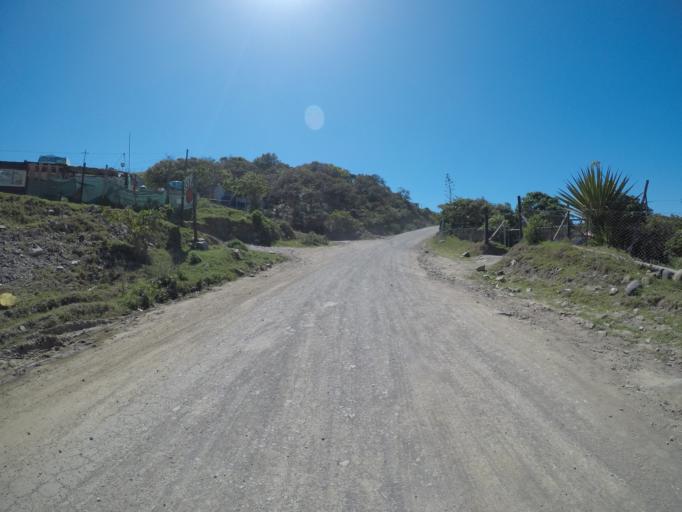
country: ZA
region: Eastern Cape
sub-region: OR Tambo District Municipality
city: Libode
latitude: -31.9873
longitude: 29.1453
